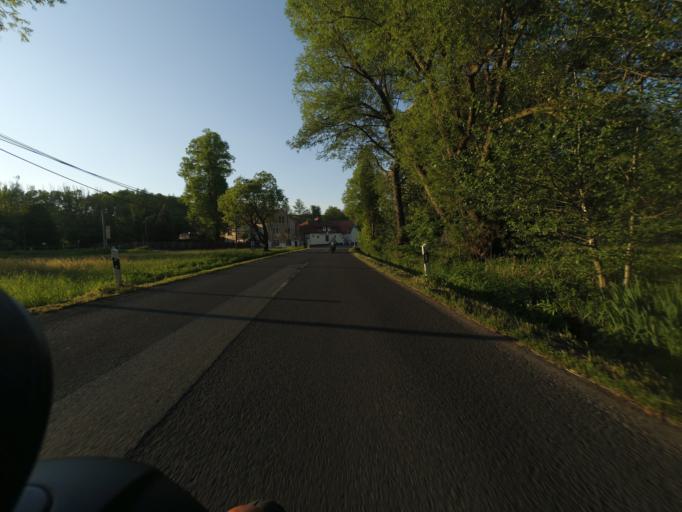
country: DE
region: Saxony
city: Kreischa
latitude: 50.9661
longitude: 13.7777
